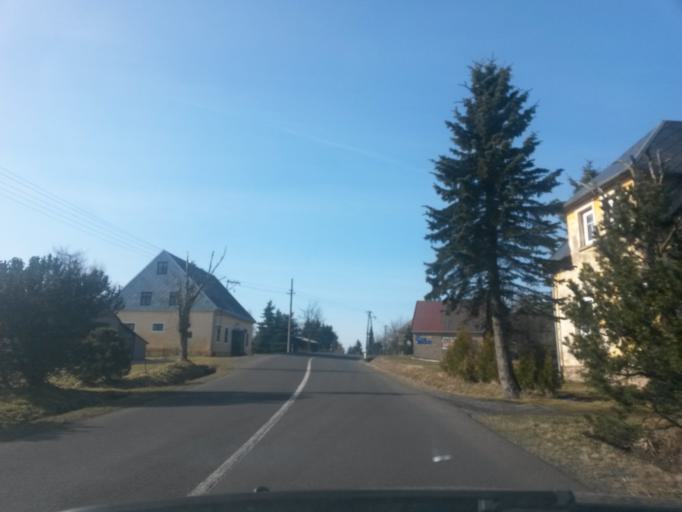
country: CZ
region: Ustecky
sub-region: Okres Chomutov
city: Kovarska
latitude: 50.4166
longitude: 13.0845
